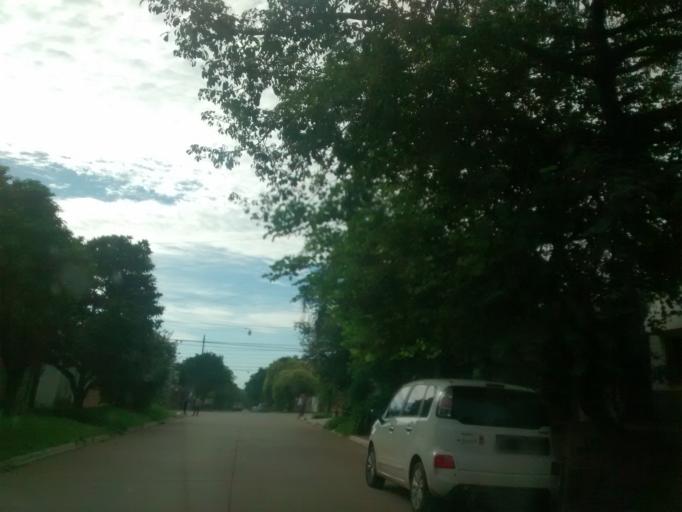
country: AR
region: Chaco
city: Resistencia
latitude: -27.4466
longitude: -58.9738
